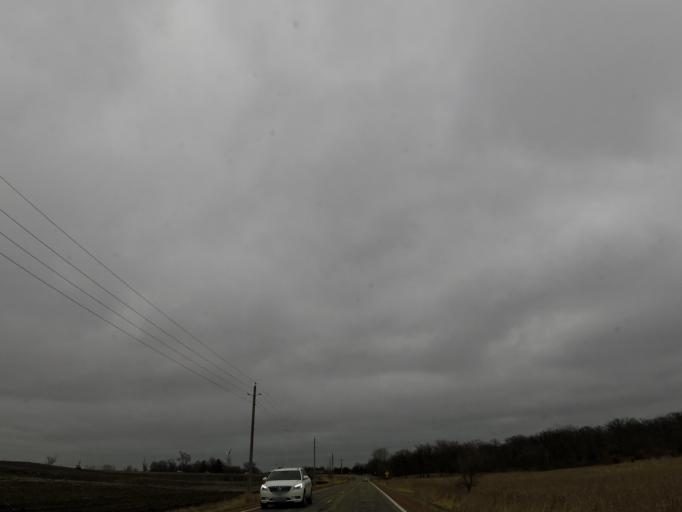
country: US
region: Minnesota
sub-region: Scott County
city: Shakopee
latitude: 44.7322
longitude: -93.5038
